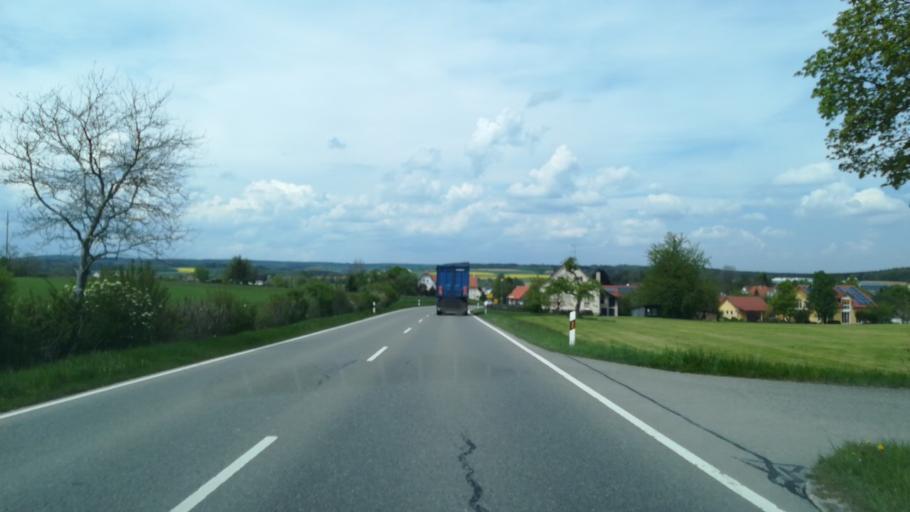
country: DE
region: Baden-Wuerttemberg
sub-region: Freiburg Region
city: Muhlingen
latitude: 47.9572
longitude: 9.0445
